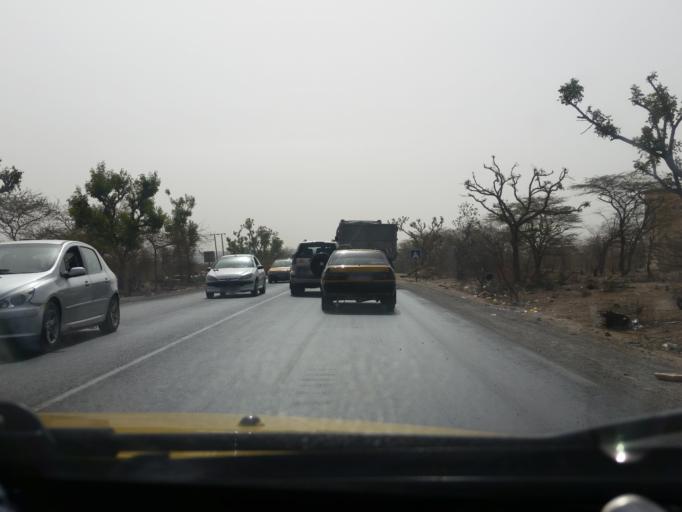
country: SN
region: Thies
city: Pout
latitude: 14.7640
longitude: -17.0170
